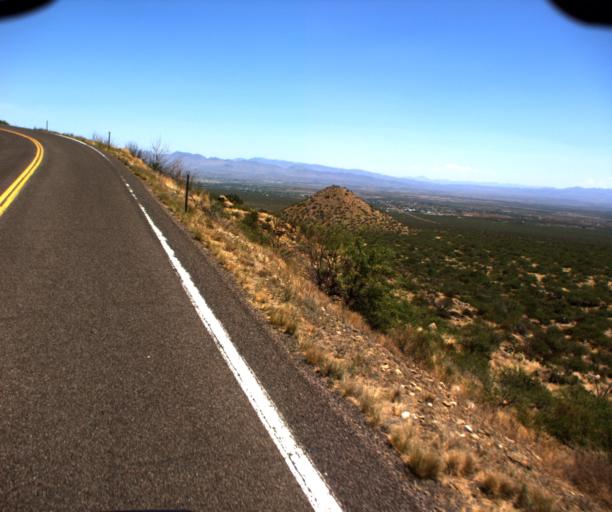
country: US
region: Arizona
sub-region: Graham County
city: Swift Trail Junction
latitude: 32.6883
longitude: -109.7602
